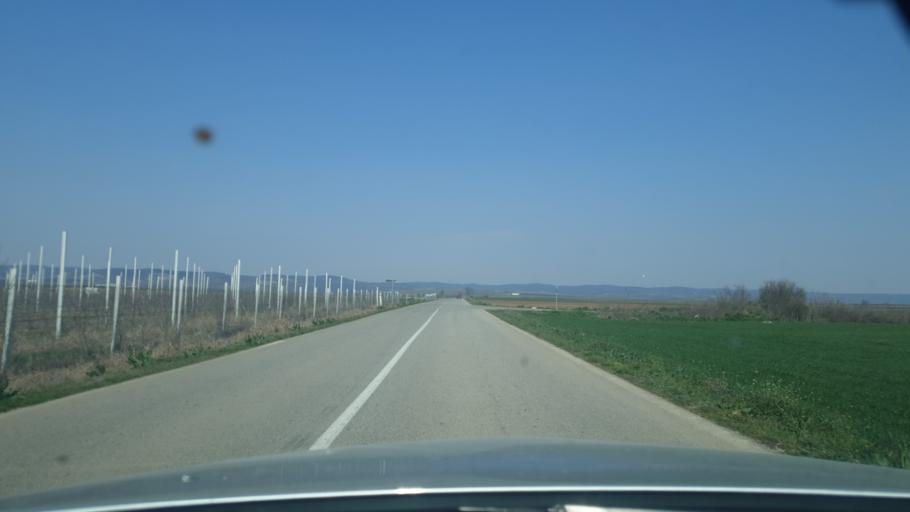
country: RS
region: Autonomna Pokrajina Vojvodina
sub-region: Sremski Okrug
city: Ruma
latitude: 45.0512
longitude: 19.7651
